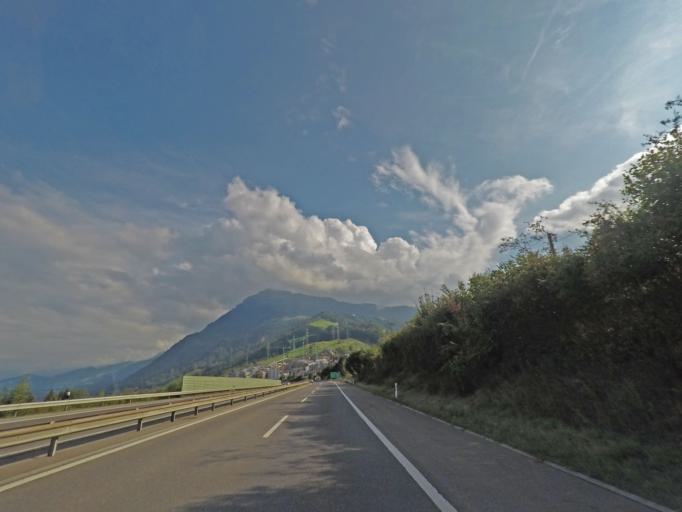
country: CH
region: Schwyz
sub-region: Bezirk Kuessnacht
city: Kussnacht
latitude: 47.0969
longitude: 8.4584
